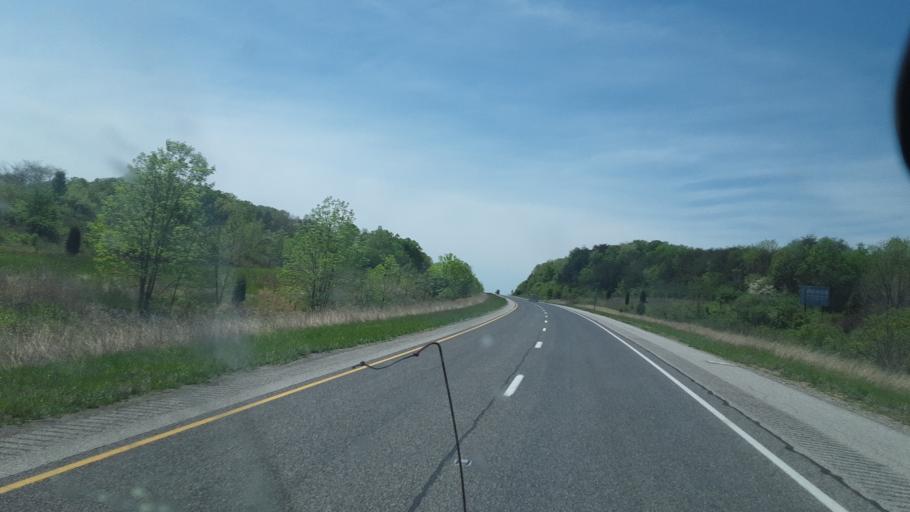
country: US
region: Indiana
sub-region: Dubois County
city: Ferdinand
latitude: 38.2160
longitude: -86.7397
